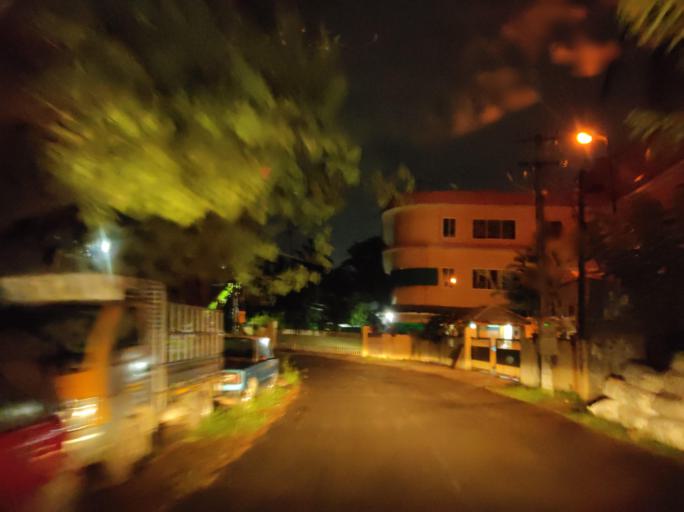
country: IN
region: Kerala
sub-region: Alappuzha
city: Arukutti
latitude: 9.8914
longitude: 76.3142
